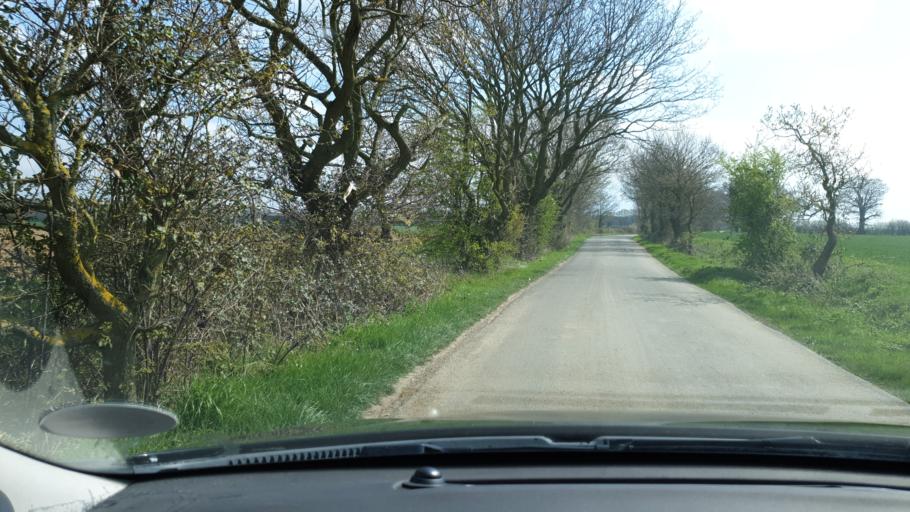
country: GB
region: England
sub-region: Essex
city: Great Bentley
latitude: 51.8412
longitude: 1.0790
